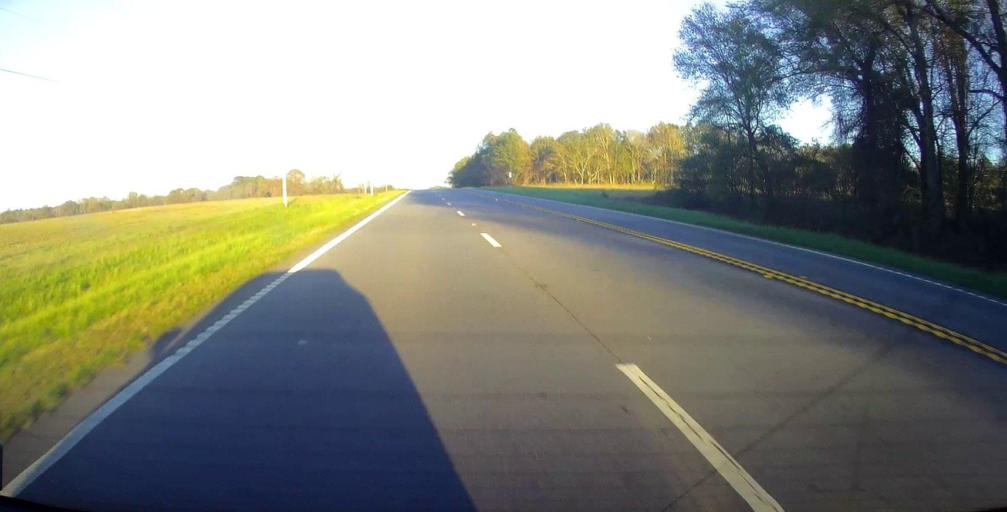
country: US
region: Georgia
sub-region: Crisp County
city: Cordele
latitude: 31.9570
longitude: -83.6389
